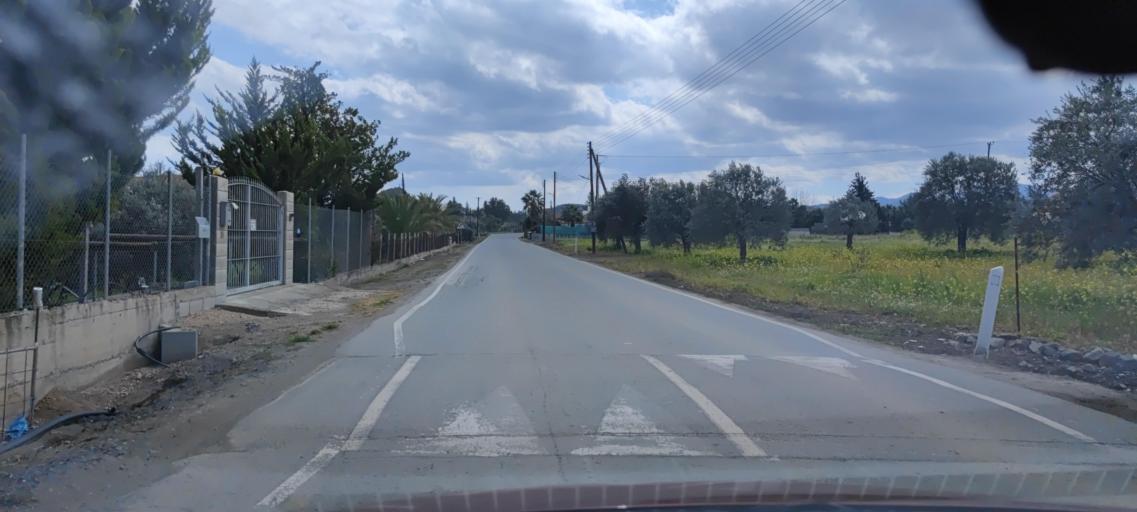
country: CY
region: Lefkosia
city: Pera
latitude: 35.0122
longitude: 33.2924
